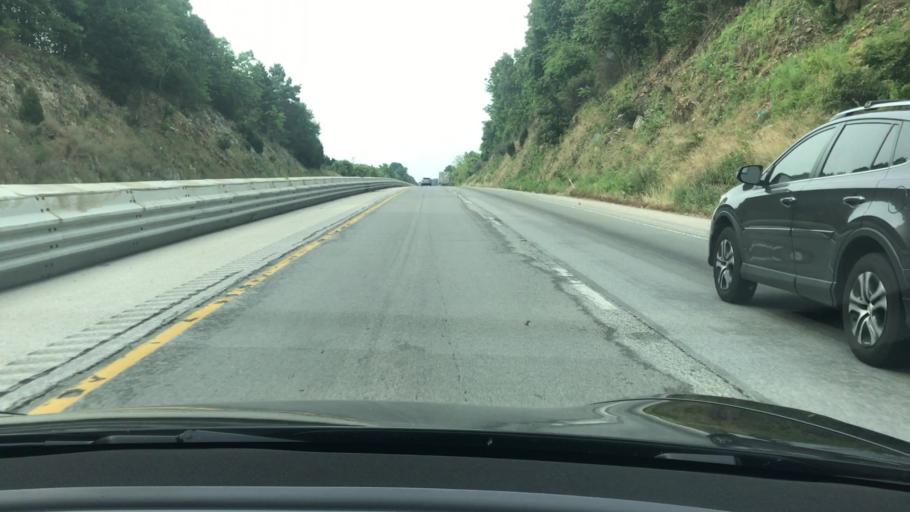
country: US
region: Pennsylvania
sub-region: York County
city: Loganville
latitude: 39.8430
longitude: -76.6880
